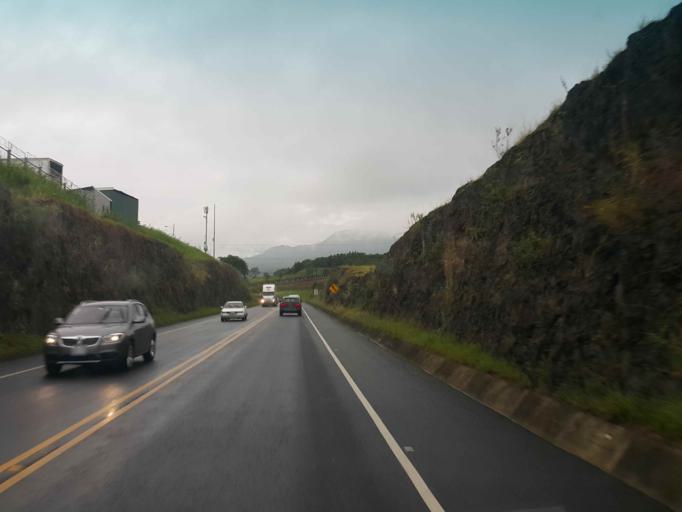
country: CR
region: Heredia
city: Colon
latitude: 9.9450
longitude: -84.2303
